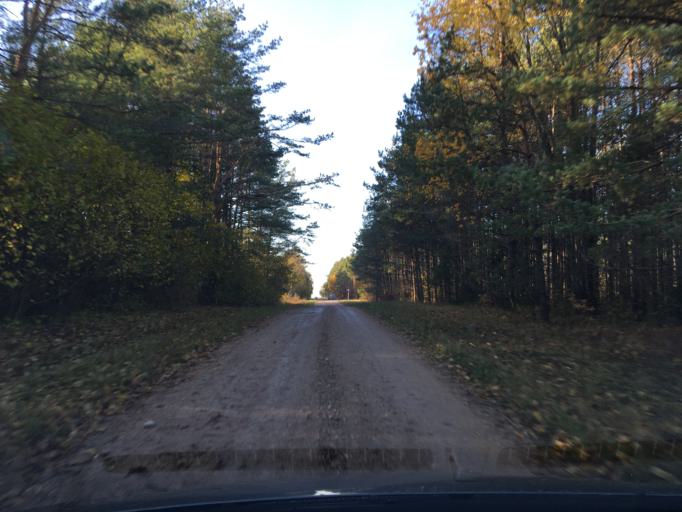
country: EE
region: Laeaene
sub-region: Lihula vald
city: Lihula
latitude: 58.5691
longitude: 23.7524
